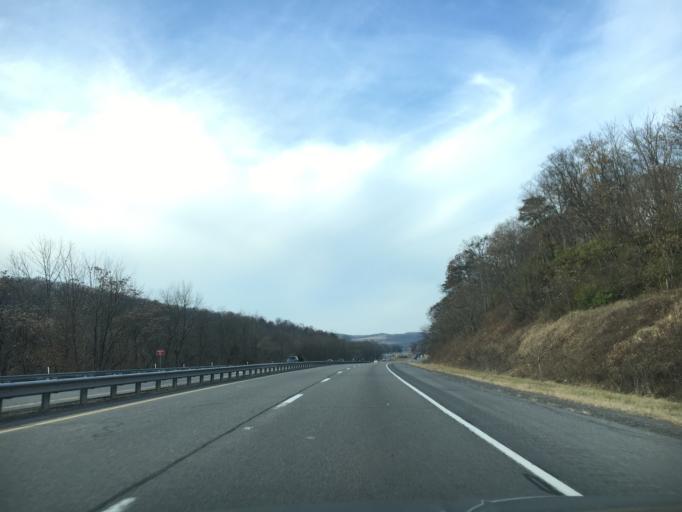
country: US
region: Pennsylvania
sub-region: Montour County
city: Danville
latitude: 40.9778
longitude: -76.6230
